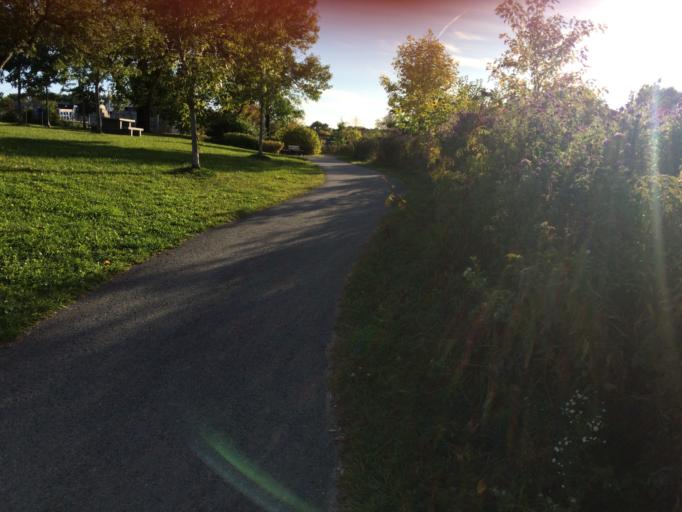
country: CA
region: Quebec
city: Quebec
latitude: 46.8123
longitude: -71.2512
